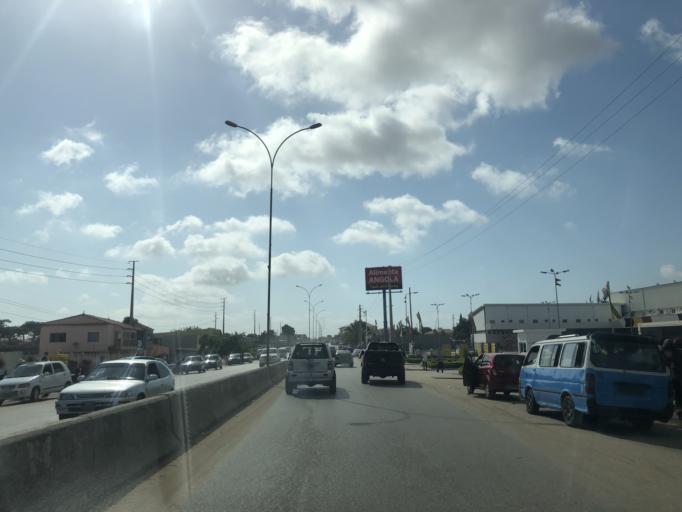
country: AO
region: Luanda
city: Luanda
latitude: -8.9018
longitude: 13.2599
